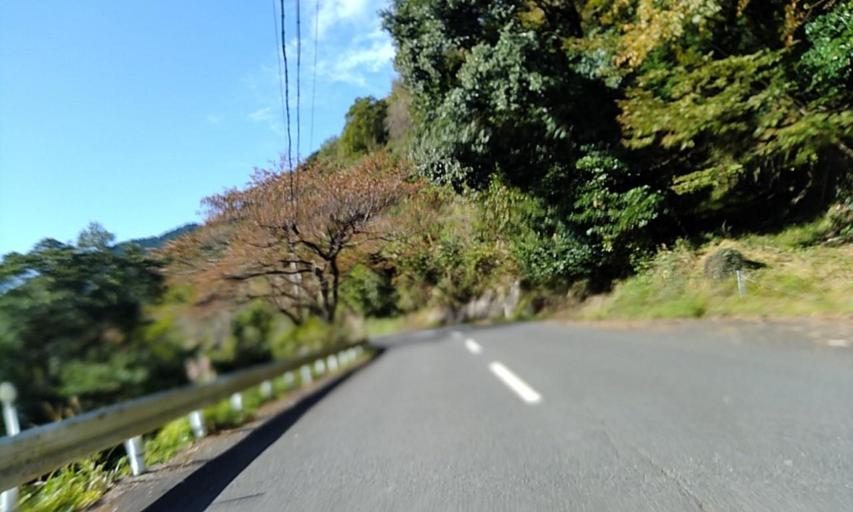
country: JP
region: Wakayama
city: Iwade
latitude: 34.0887
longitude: 135.3642
